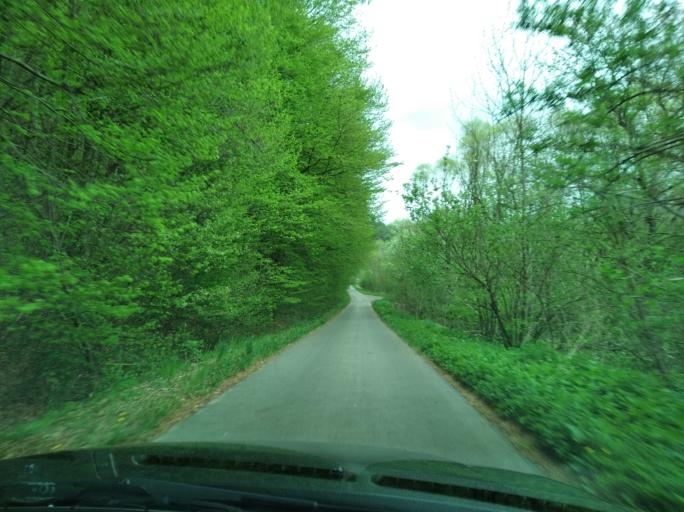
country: PL
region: Subcarpathian Voivodeship
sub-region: Powiat brzozowski
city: Dydnia
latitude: 49.6585
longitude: 22.2630
